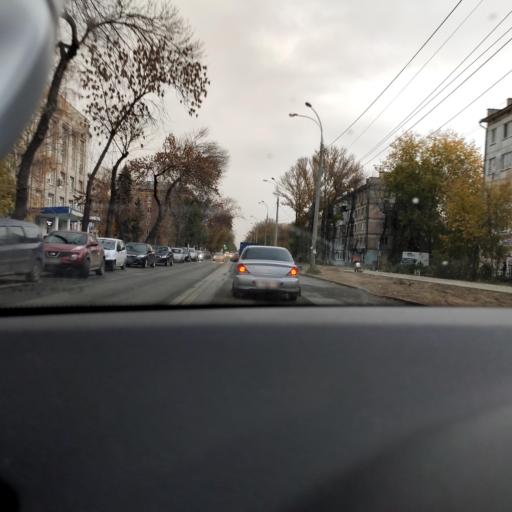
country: RU
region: Samara
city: Samara
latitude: 53.2099
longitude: 50.2469
